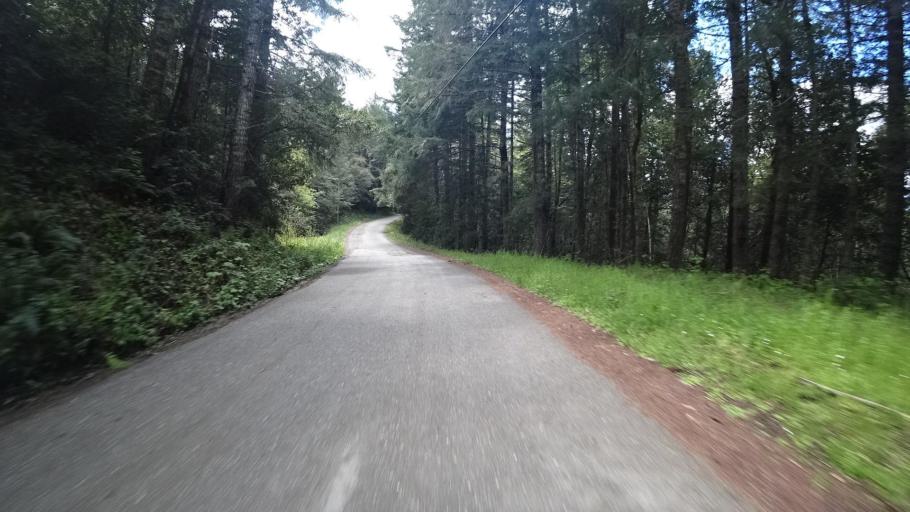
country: US
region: California
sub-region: Humboldt County
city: Blue Lake
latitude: 40.7936
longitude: -123.8770
